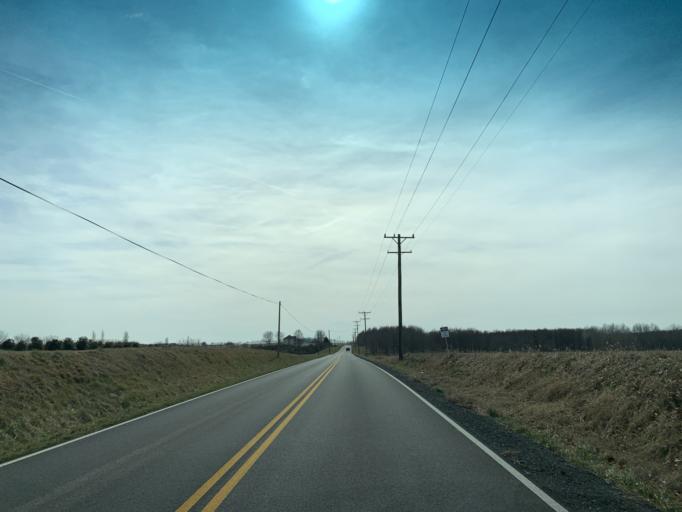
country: US
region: Maryland
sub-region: Frederick County
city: Adamstown
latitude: 39.2828
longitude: -77.4701
